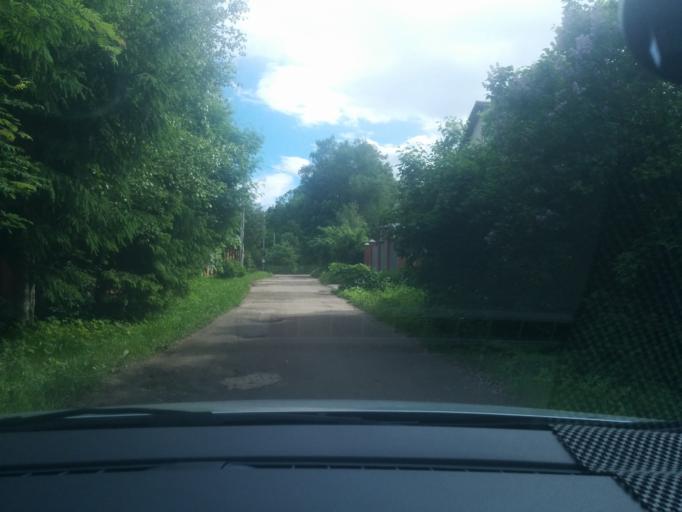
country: RU
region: Moskovskaya
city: Lugovaya
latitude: 56.0524
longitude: 37.4968
